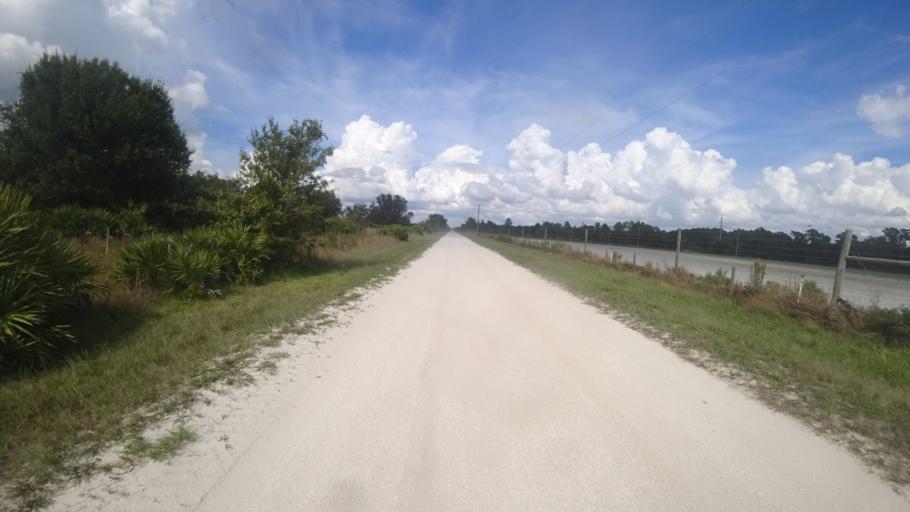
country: US
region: Florida
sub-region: Hillsborough County
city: Wimauma
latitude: 27.5522
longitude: -82.1744
